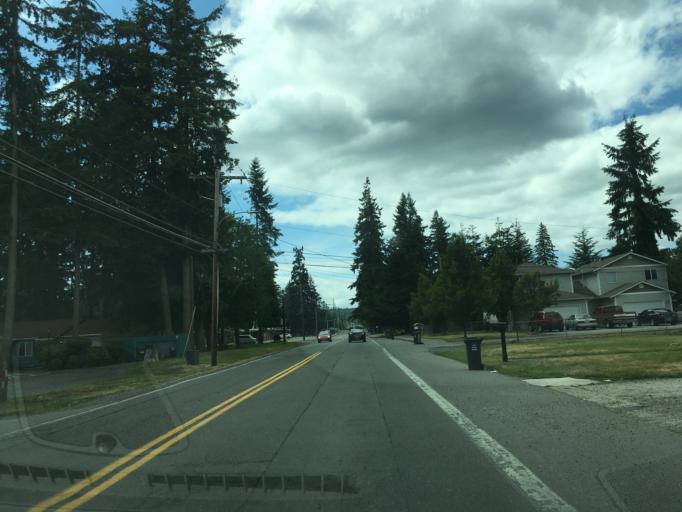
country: US
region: Washington
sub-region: Snohomish County
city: Marysville
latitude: 48.0756
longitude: -122.1715
